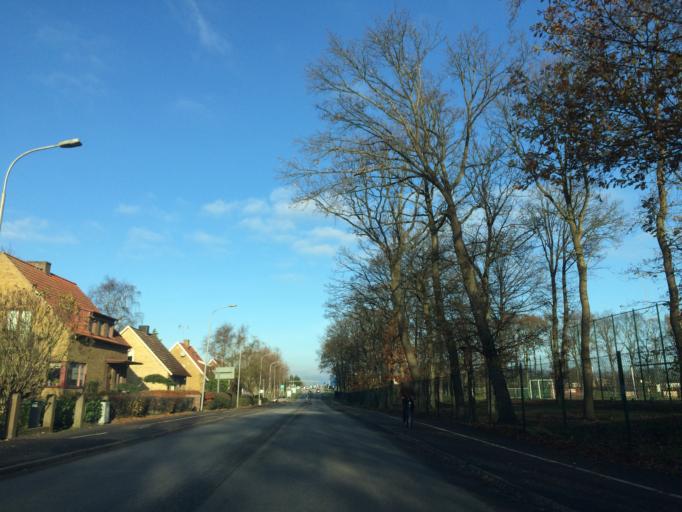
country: SE
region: Skane
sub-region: Lunds Kommun
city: Lund
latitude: 55.7167
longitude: 13.2022
